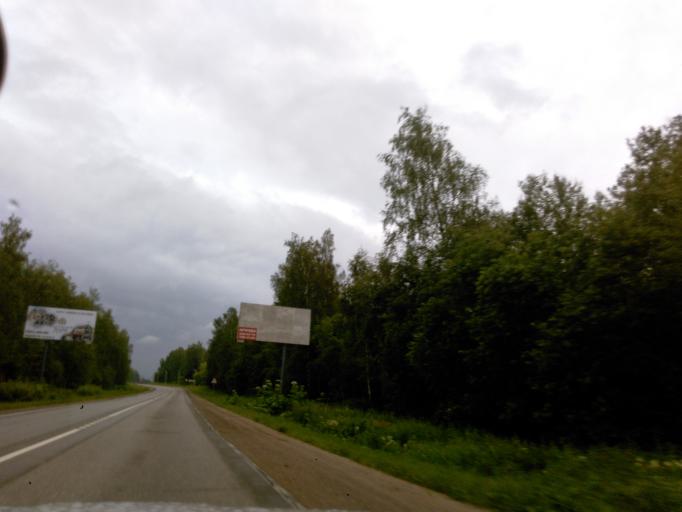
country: RU
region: Moskovskaya
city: Povarovo
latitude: 56.0304
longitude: 36.9787
